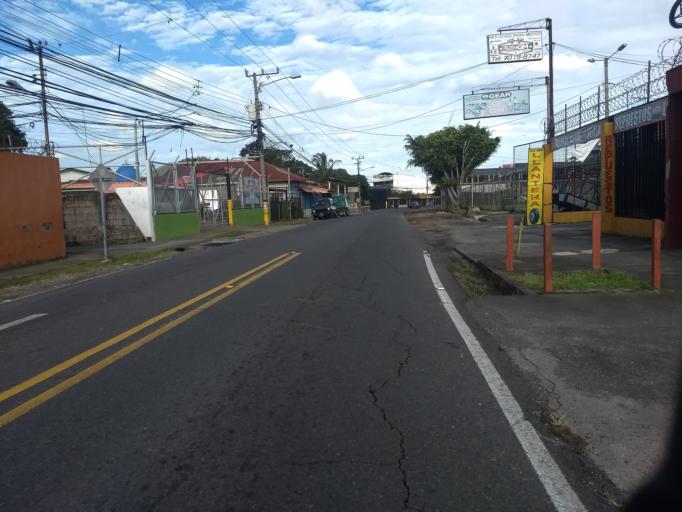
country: CR
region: San Jose
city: Colima
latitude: 9.9540
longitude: -84.0821
